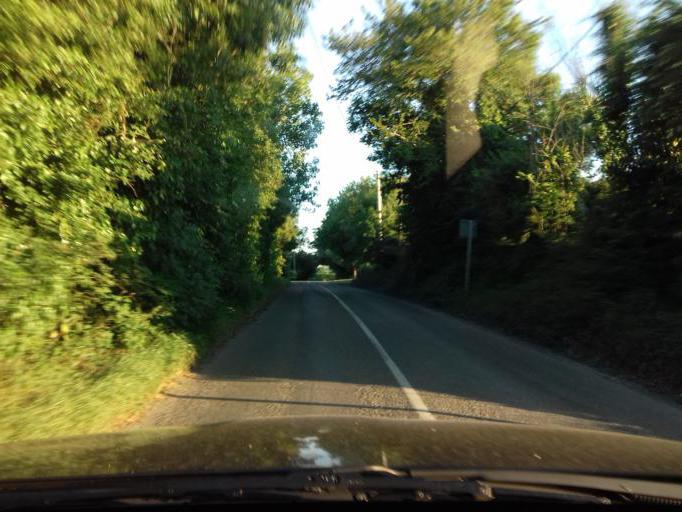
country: IE
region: Leinster
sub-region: An Mhi
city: Ashbourne
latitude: 53.4753
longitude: -6.3192
